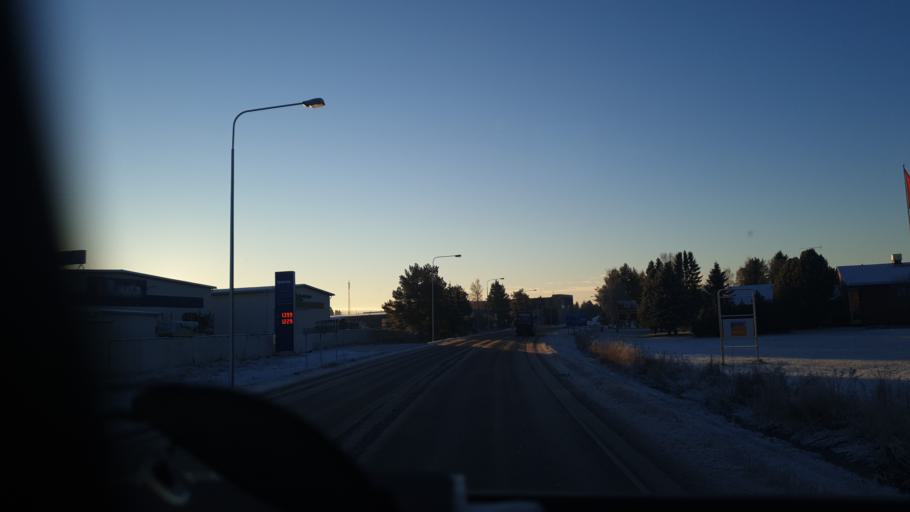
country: FI
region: Northern Ostrobothnia
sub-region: Ylivieska
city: Kalajoki
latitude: 64.2634
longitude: 23.9492
